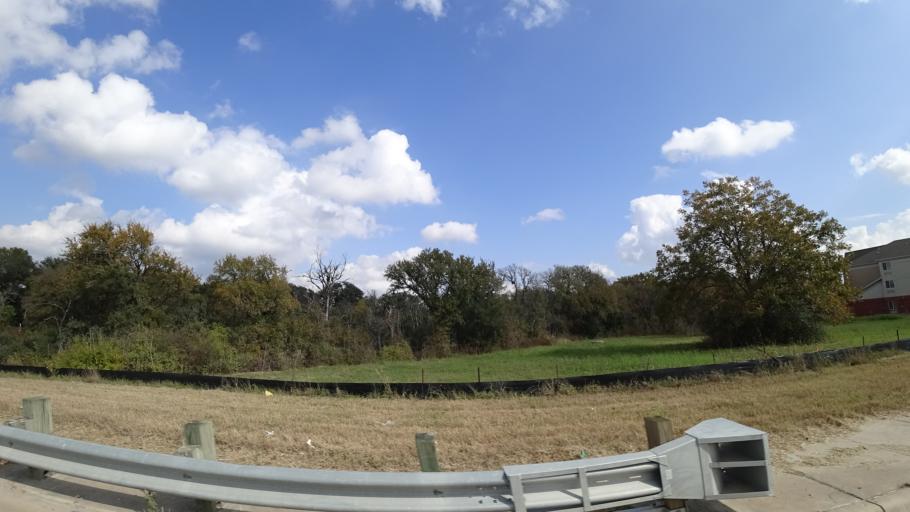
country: US
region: Texas
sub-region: Williamson County
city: Round Rock
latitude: 30.5066
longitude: -97.6842
